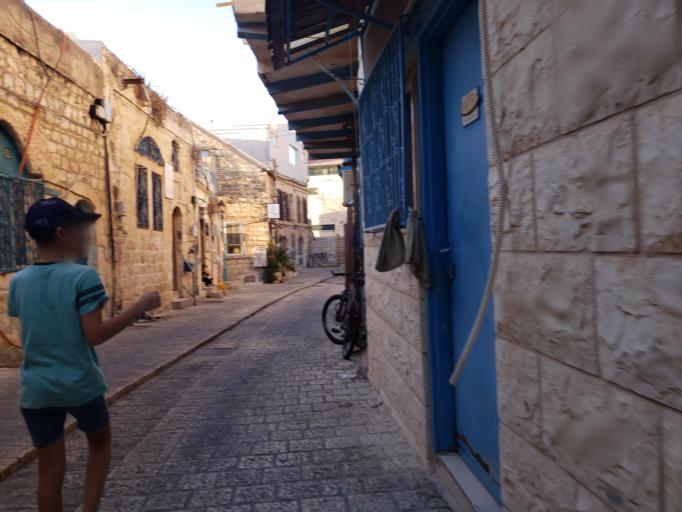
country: IL
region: Northern District
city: Safed
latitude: 32.9697
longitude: 35.4923
